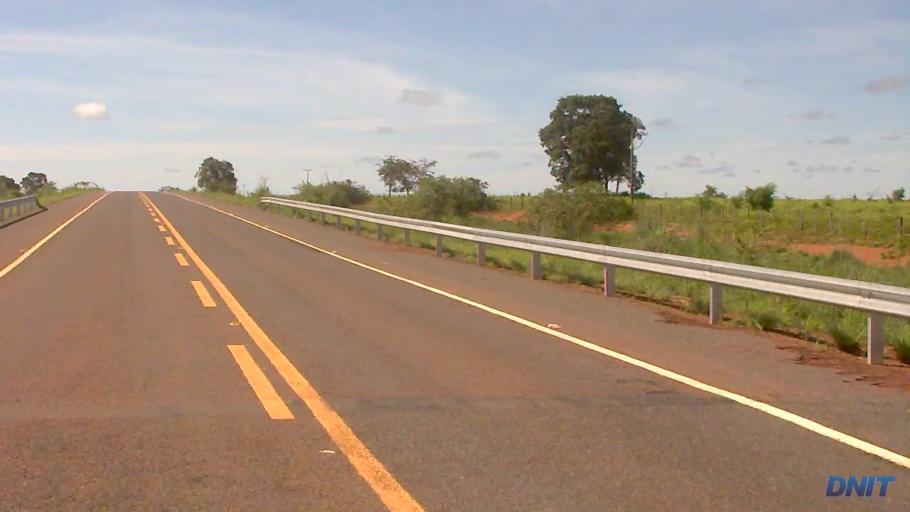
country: BR
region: Goias
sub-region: Sao Miguel Do Araguaia
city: Sao Miguel do Araguaia
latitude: -13.3654
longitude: -50.1452
